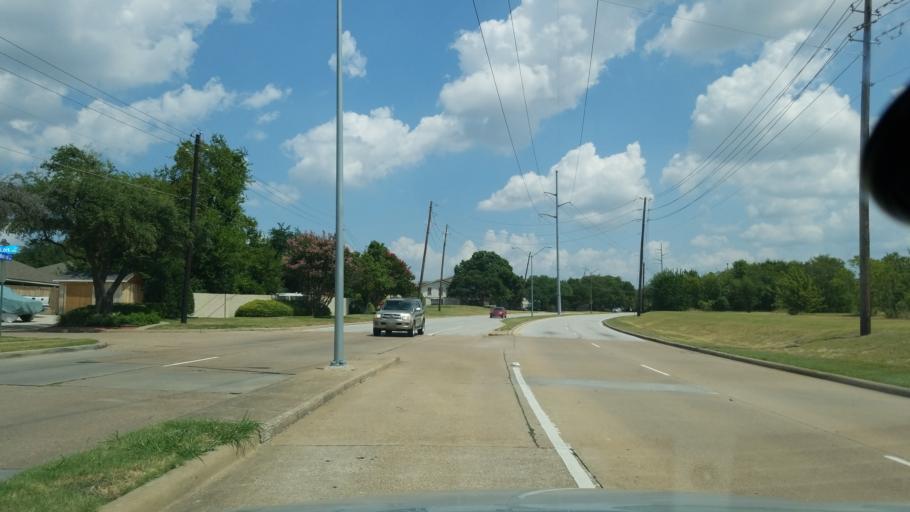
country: US
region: Texas
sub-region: Dallas County
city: Richardson
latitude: 32.9254
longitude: -96.7244
